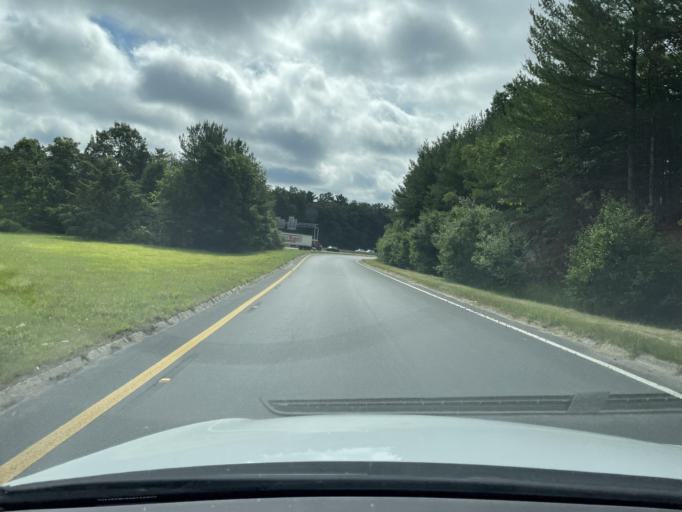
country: US
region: Massachusetts
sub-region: Middlesex County
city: Wilmington
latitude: 42.5749
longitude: -71.1522
